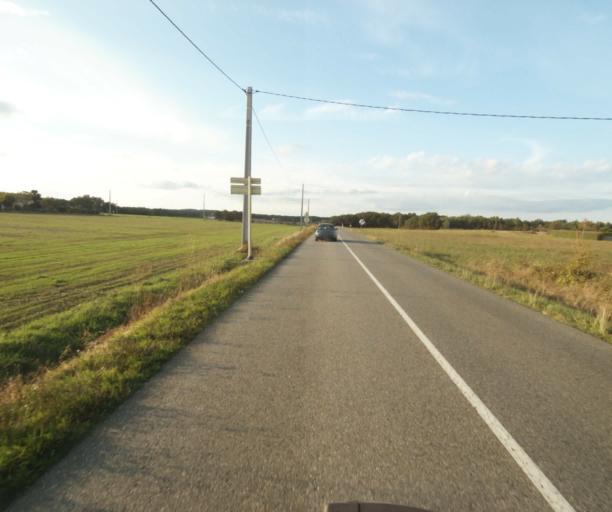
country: FR
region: Midi-Pyrenees
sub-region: Departement du Tarn-et-Garonne
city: Verdun-sur-Garonne
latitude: 43.8353
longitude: 1.1591
